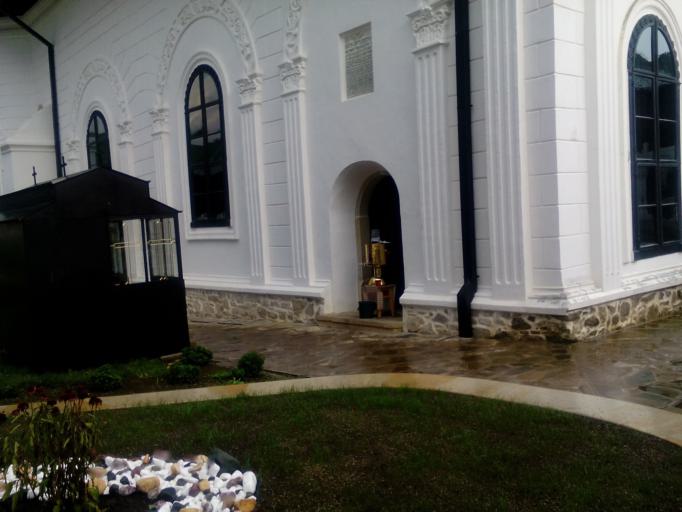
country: RO
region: Neamt
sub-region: Comuna Agapia
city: Filioara
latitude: 47.1704
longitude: 26.2351
